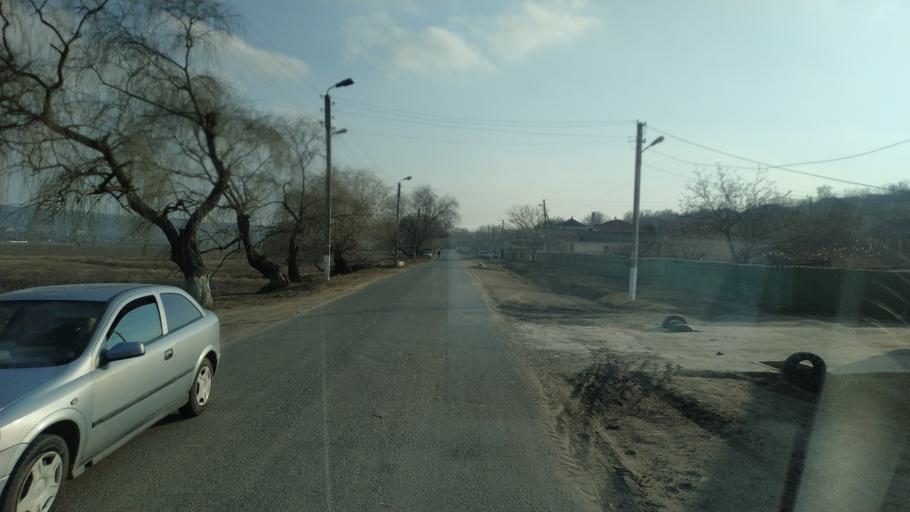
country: MD
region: Hincesti
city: Dancu
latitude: 46.7745
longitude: 28.3461
